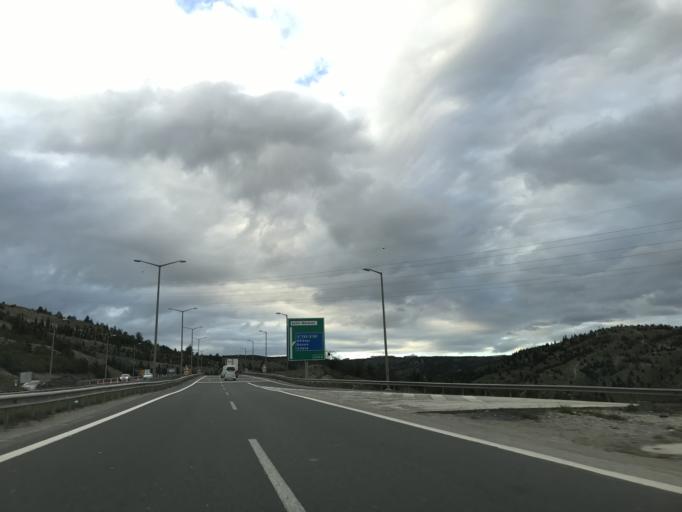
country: TR
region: Ankara
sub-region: Goelbasi
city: Golbasi
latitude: 39.8105
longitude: 32.7999
